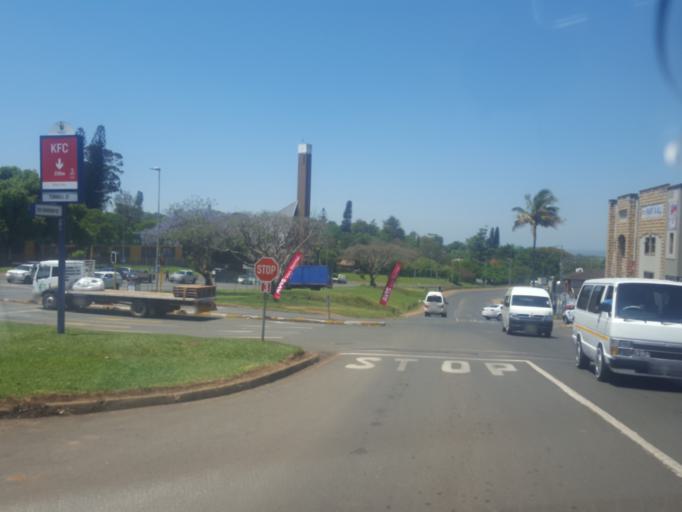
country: ZA
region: KwaZulu-Natal
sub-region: uThungulu District Municipality
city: Empangeni
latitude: -28.7460
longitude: 31.8901
